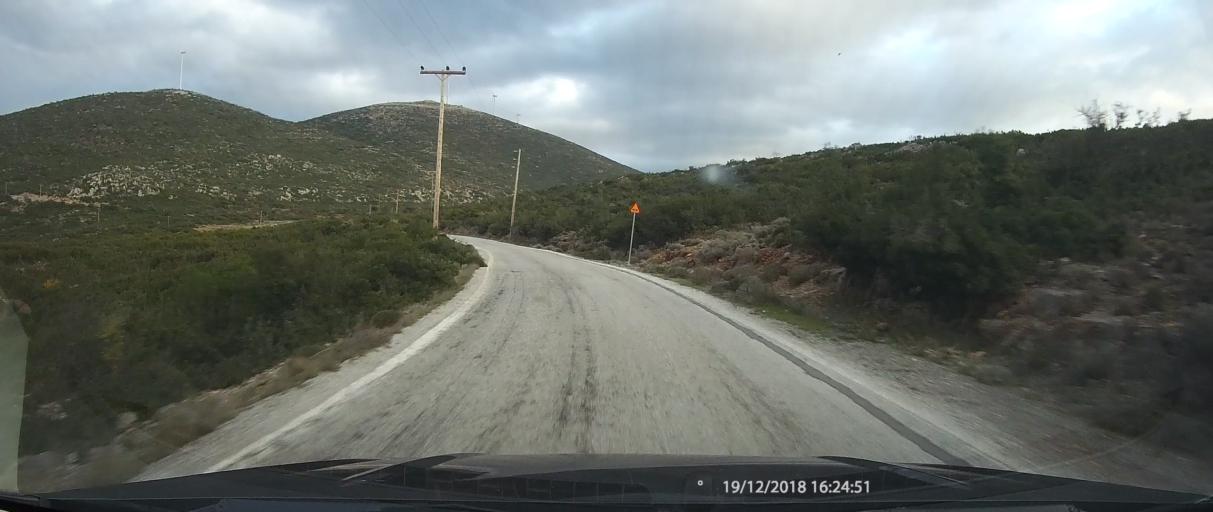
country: GR
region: Peloponnese
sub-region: Nomos Lakonias
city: Kato Glikovrisi
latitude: 36.9534
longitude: 22.8435
